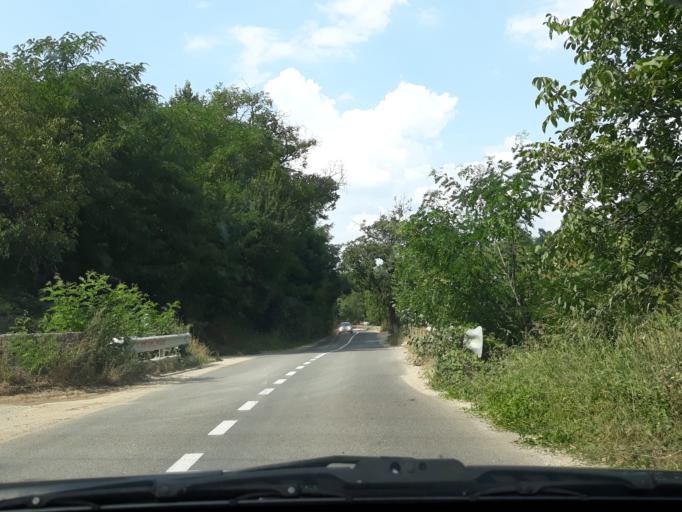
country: RO
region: Bihor
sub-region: Comuna Pietroasa
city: Pietroasa
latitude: 46.5888
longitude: 22.5637
